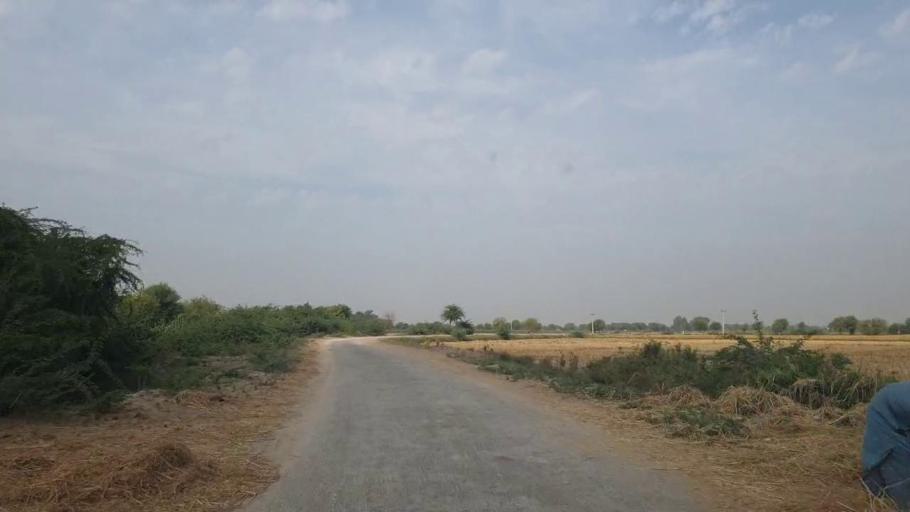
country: PK
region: Sindh
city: Rajo Khanani
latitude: 24.9378
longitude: 68.9855
